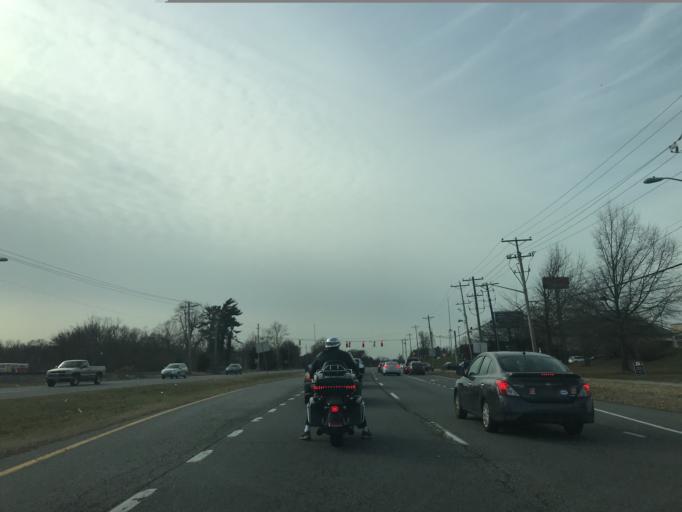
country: US
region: Delaware
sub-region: New Castle County
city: Bear
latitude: 39.6512
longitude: -75.6214
